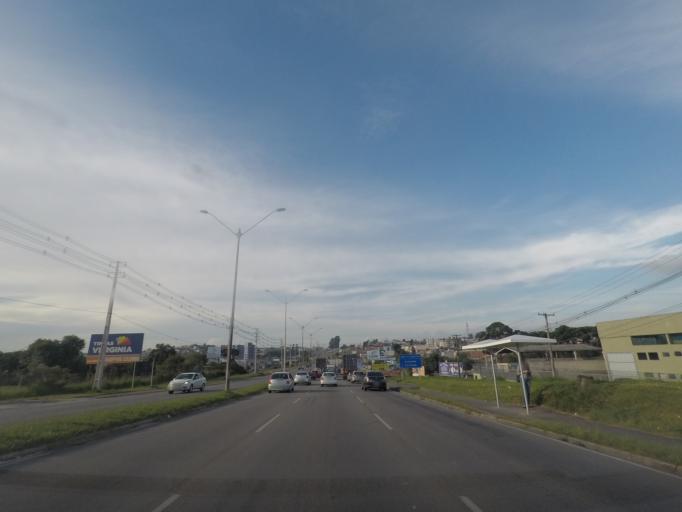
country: BR
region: Parana
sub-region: Pinhais
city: Pinhais
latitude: -25.3783
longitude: -49.1968
